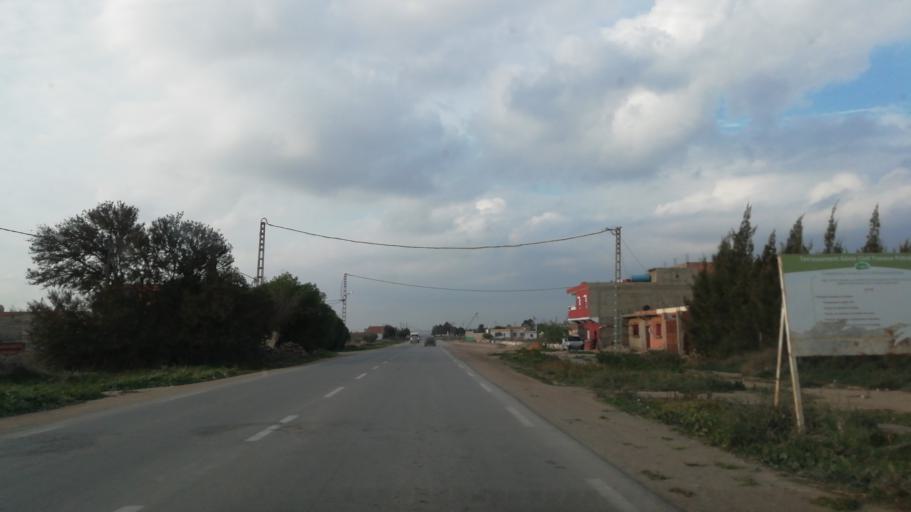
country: DZ
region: Mascara
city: Sig
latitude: 35.6898
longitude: -0.0172
